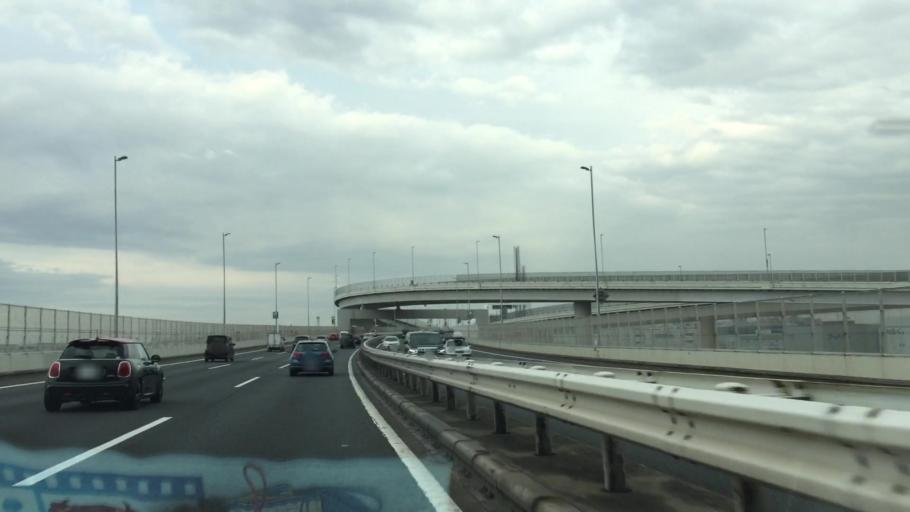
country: JP
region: Kanagawa
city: Yokohama
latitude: 35.4636
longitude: 139.6810
